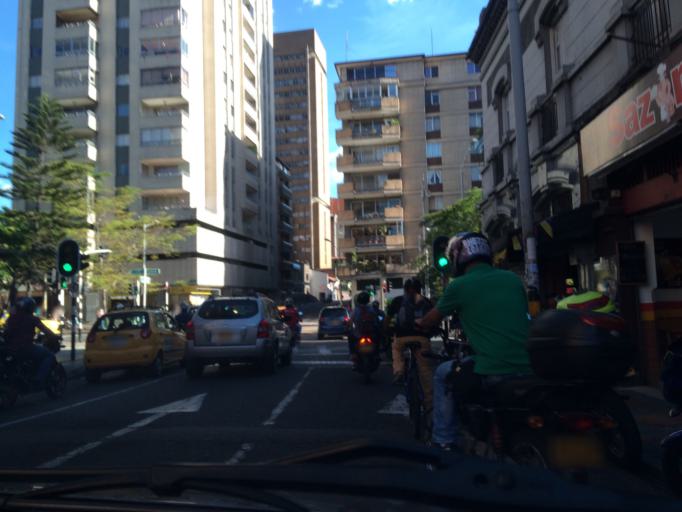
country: CO
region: Antioquia
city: Medellin
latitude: 6.2486
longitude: -75.5621
